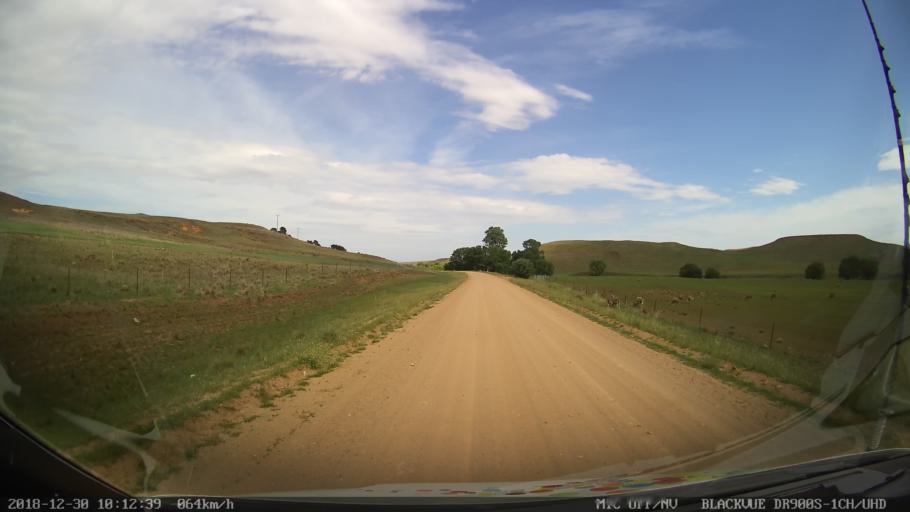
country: AU
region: New South Wales
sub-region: Snowy River
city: Berridale
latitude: -36.5404
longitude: 149.0737
